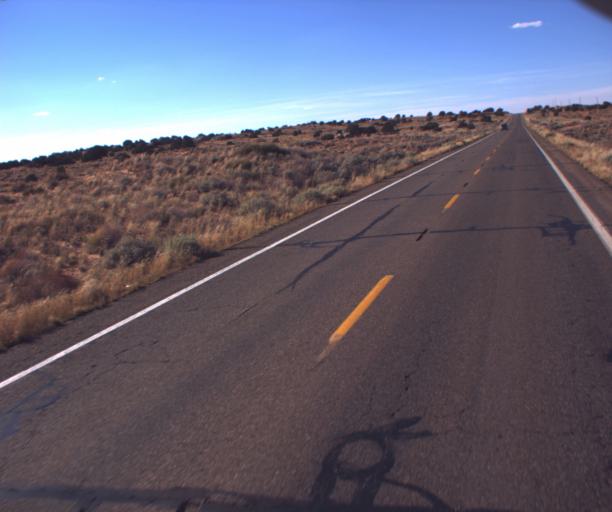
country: US
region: Arizona
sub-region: Coconino County
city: Kaibito
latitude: 36.5893
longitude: -111.1554
